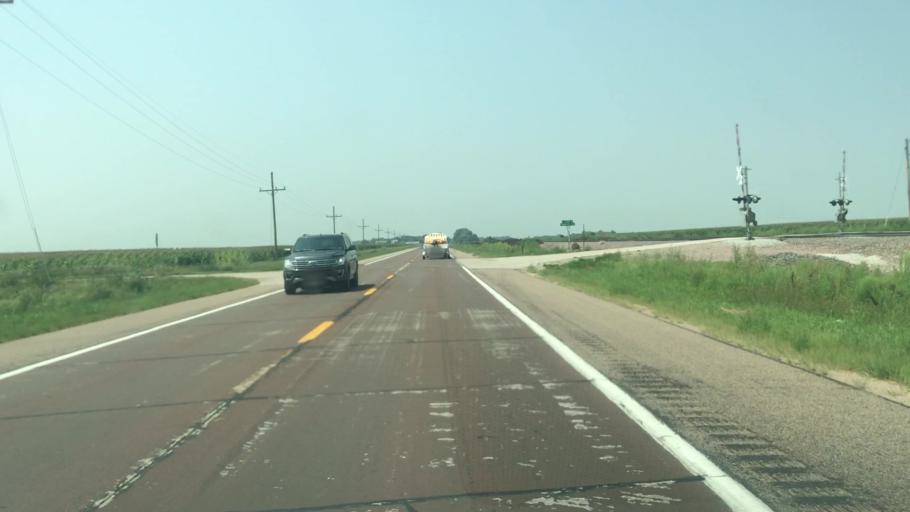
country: US
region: Nebraska
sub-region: Hall County
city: Grand Island
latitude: 40.9648
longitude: -98.4355
